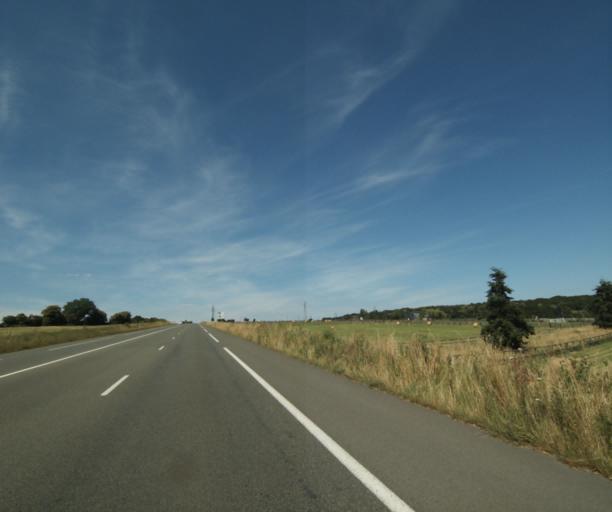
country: FR
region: Pays de la Loire
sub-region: Departement de la Mayenne
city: Montigne-le-Brillant
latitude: 48.0382
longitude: -0.8028
